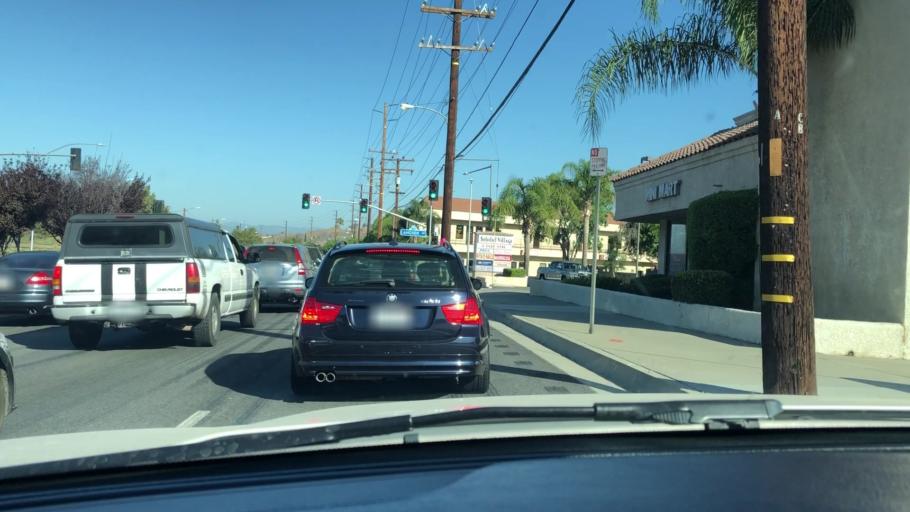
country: US
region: California
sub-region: Los Angeles County
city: Santa Clarita
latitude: 34.4206
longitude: -118.4841
